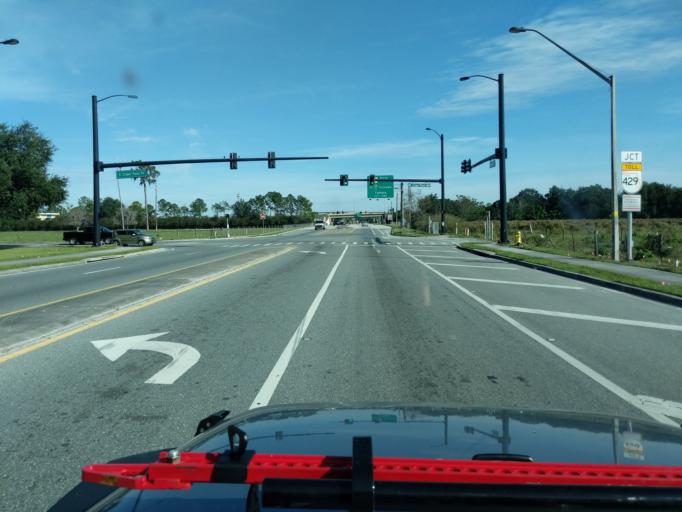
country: US
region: Florida
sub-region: Orange County
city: Ocoee
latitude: 28.5718
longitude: -81.5614
